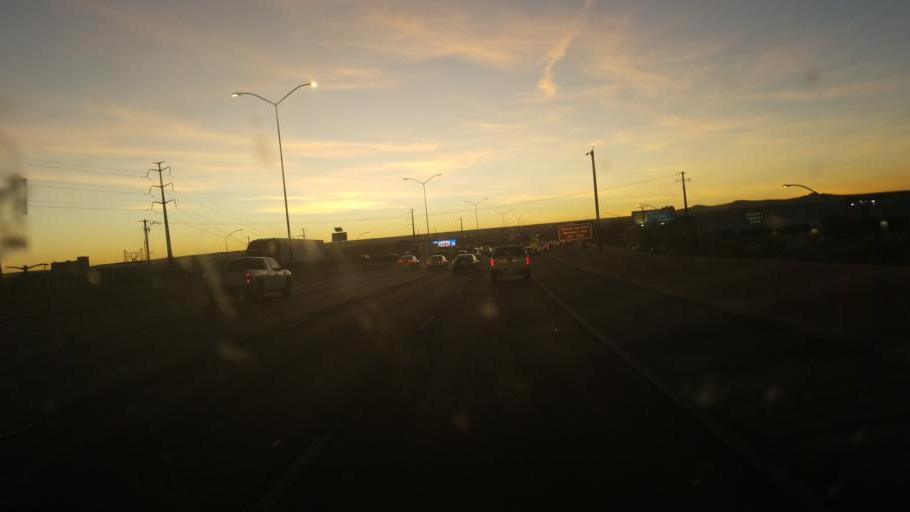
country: US
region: New Mexico
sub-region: Bernalillo County
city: Albuquerque
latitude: 35.1065
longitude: -106.6587
